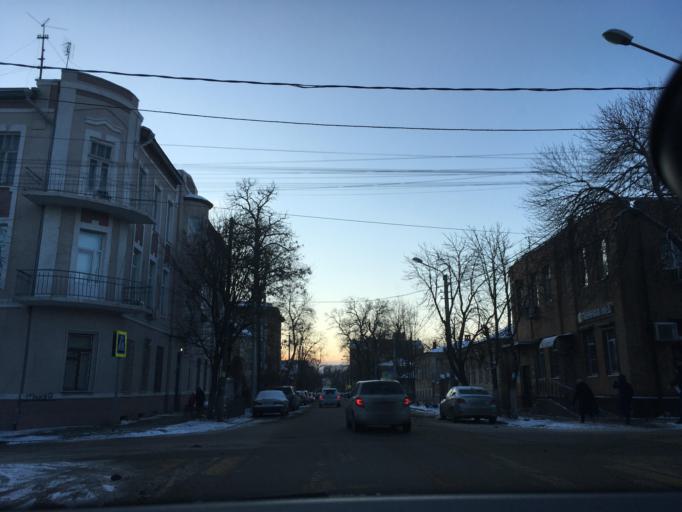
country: RU
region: Rostov
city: Rostov-na-Donu
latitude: 47.2312
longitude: 39.7561
